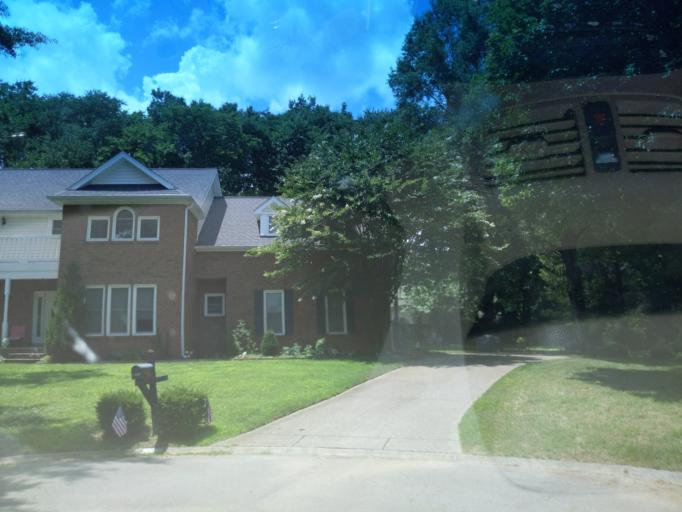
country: US
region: Tennessee
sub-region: Williamson County
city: Brentwood
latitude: 36.0446
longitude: -86.7637
